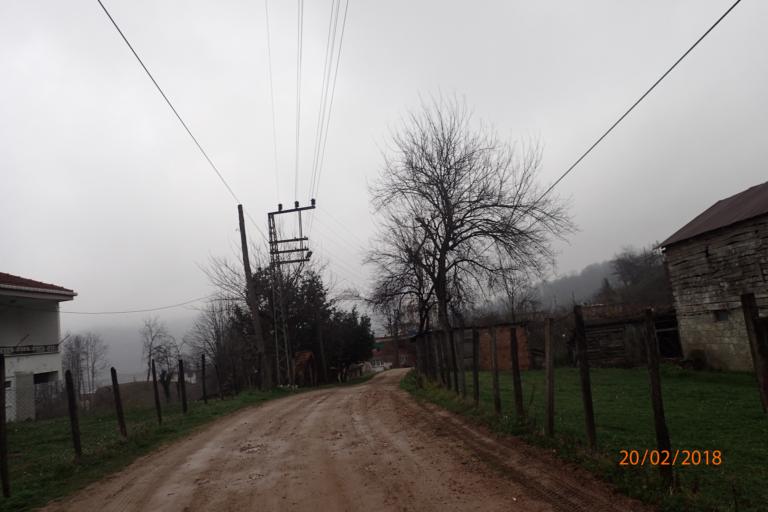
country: TR
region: Ordu
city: Camas
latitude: 40.9480
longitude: 37.5202
